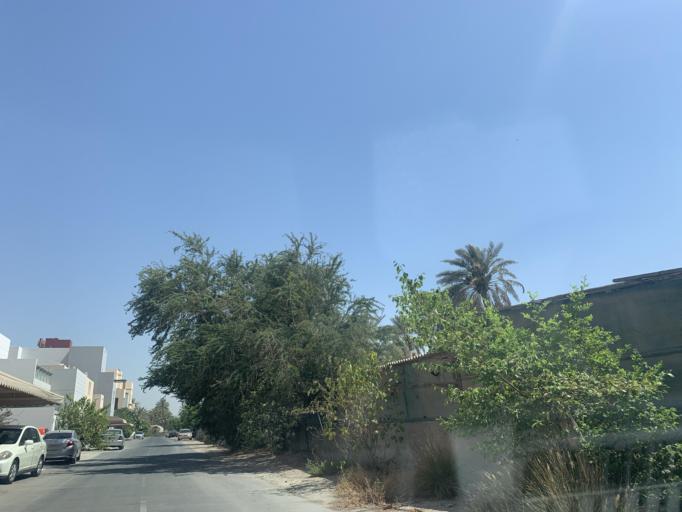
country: BH
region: Manama
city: Jidd Hafs
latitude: 26.2274
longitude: 50.5054
